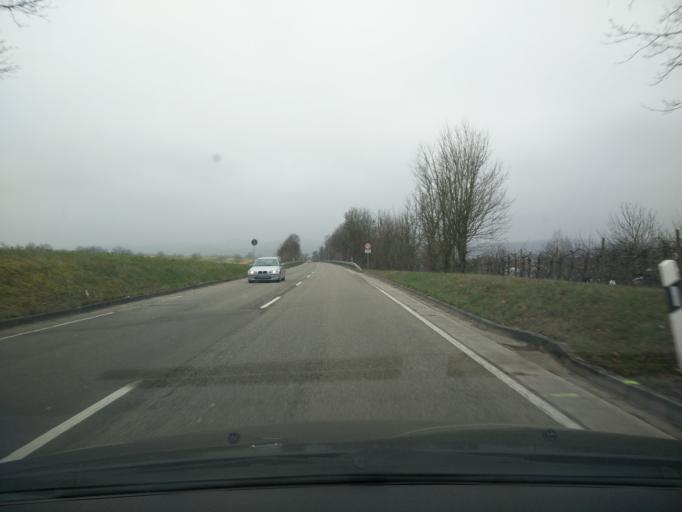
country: DE
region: Rheinland-Pfalz
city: Kapellen-Drusweiler
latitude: 49.1009
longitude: 8.0372
